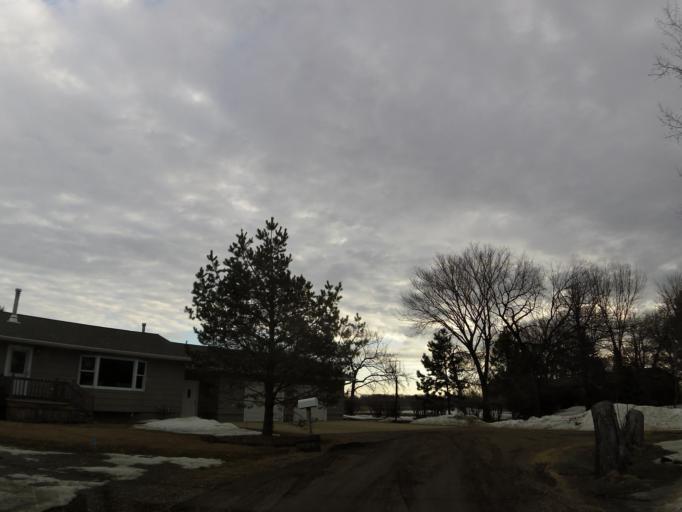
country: US
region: North Dakota
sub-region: Walsh County
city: Grafton
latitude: 48.4212
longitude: -97.4352
